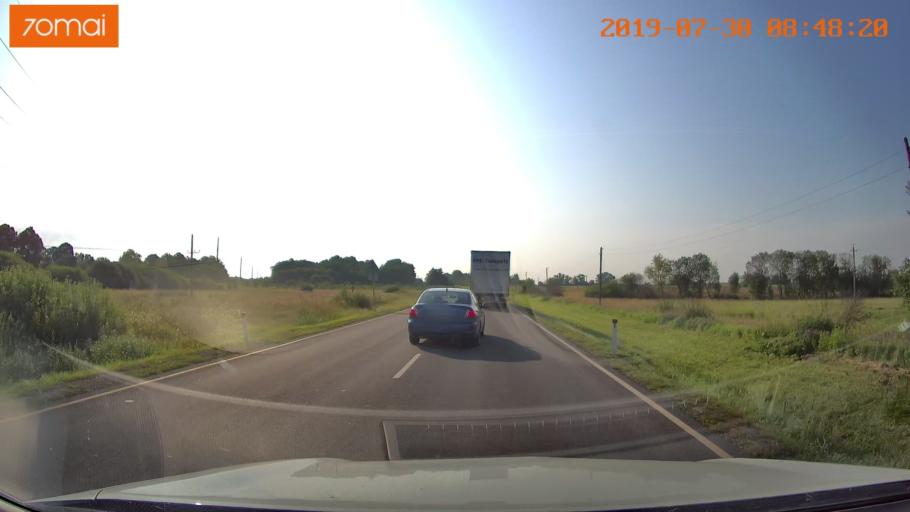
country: RU
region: Kaliningrad
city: Chernyakhovsk
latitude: 54.6183
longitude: 21.9041
